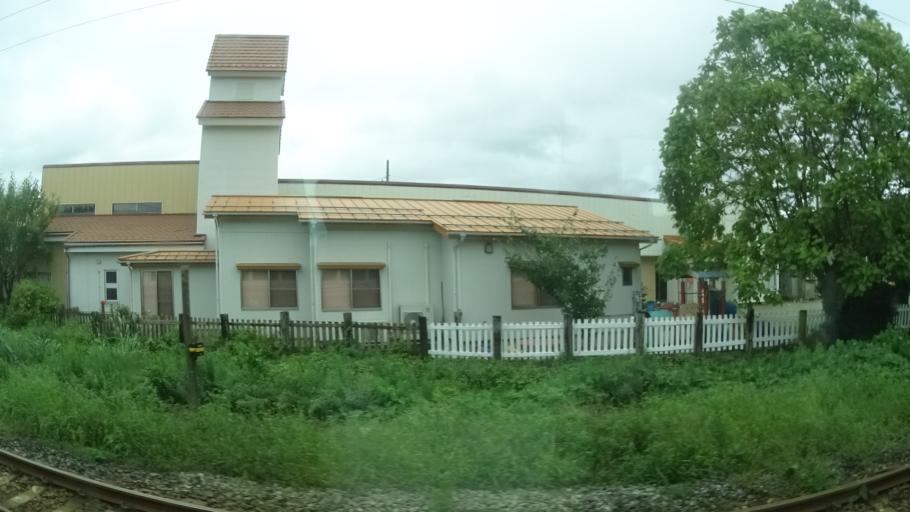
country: JP
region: Niigata
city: Murakami
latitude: 38.2157
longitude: 139.4634
